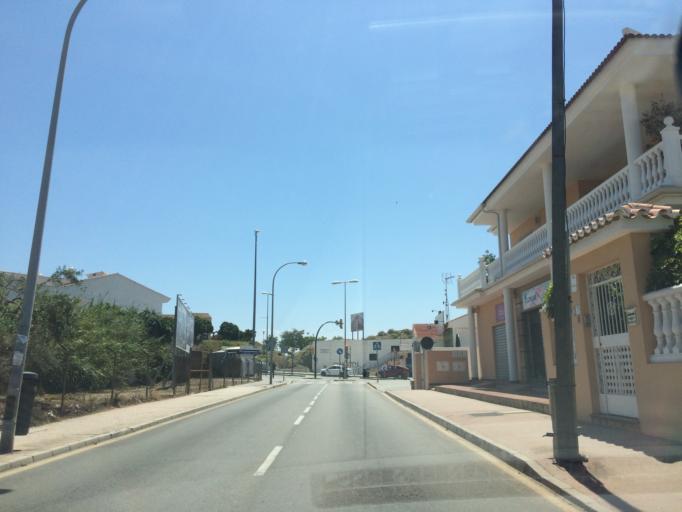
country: ES
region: Andalusia
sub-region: Provincia de Malaga
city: Malaga
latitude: 36.7407
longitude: -4.4827
